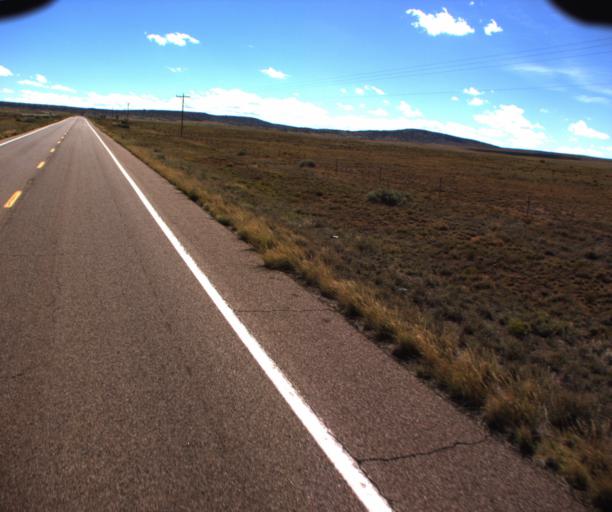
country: US
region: Arizona
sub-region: Apache County
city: Saint Johns
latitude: 34.5054
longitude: -109.6212
